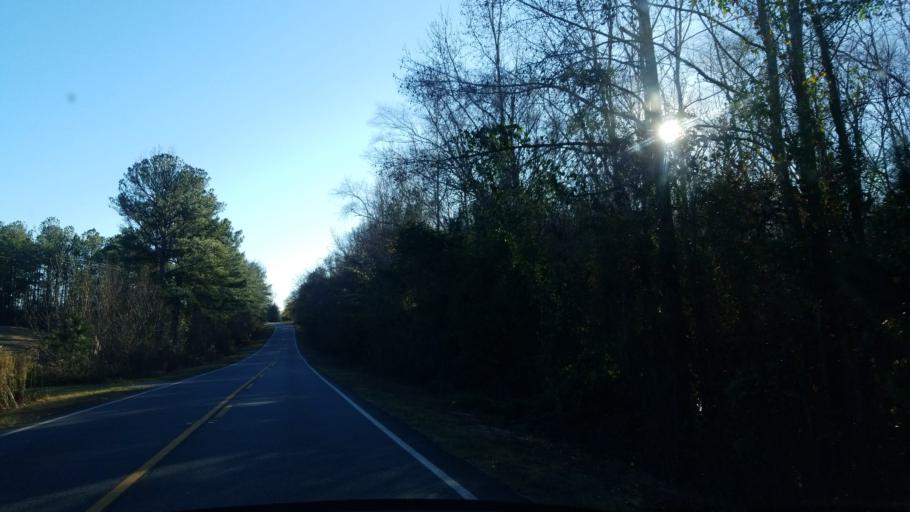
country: US
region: Georgia
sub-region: Talbot County
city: Talbotton
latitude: 32.5418
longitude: -84.6020
